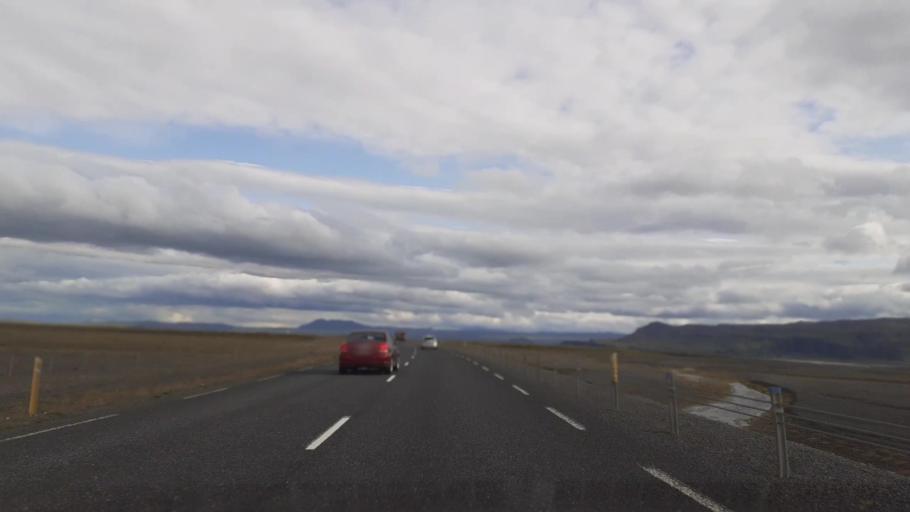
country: IS
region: South
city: Vestmannaeyjar
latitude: 63.5588
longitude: -20.0647
